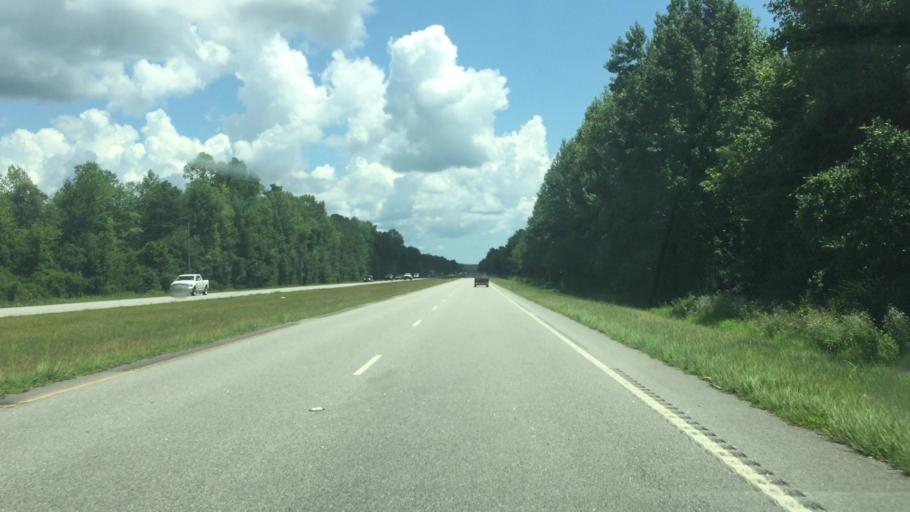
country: US
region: South Carolina
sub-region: Horry County
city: Loris
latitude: 34.0442
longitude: -78.8280
